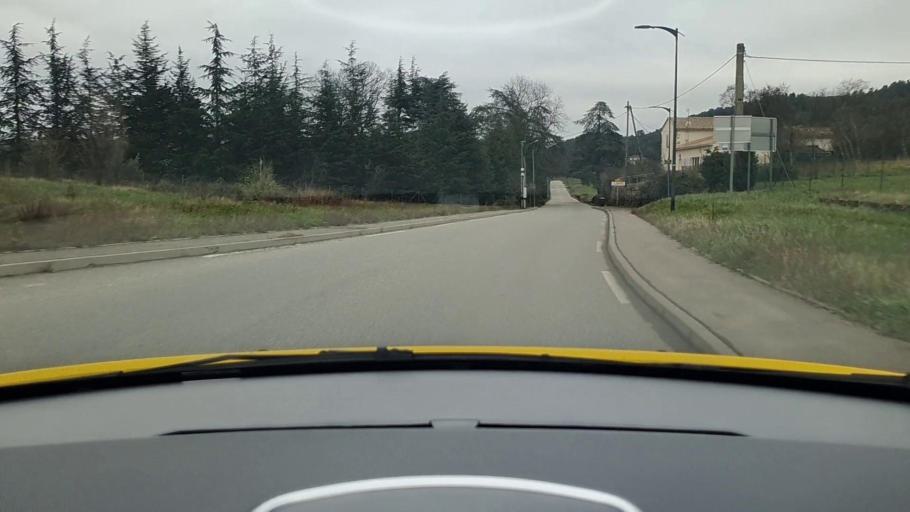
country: FR
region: Languedoc-Roussillon
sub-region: Departement du Gard
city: Laval-Pradel
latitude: 44.2292
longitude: 4.0617
